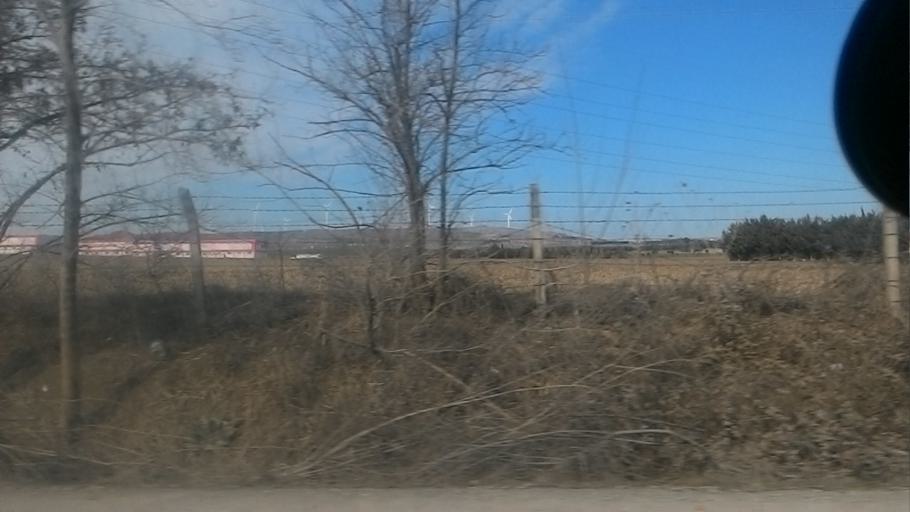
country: TR
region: Istanbul
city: Canta
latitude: 41.0804
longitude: 28.0577
